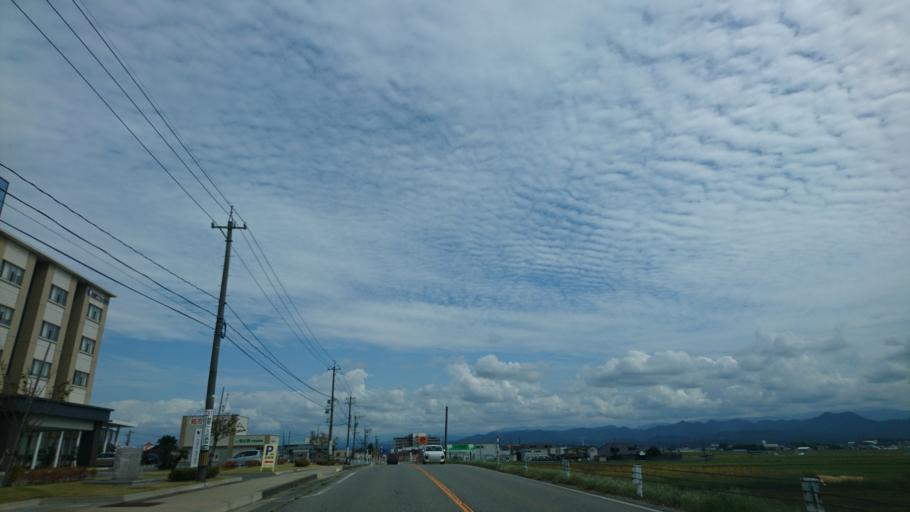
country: JP
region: Ishikawa
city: Komatsu
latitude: 36.3173
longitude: 136.3431
